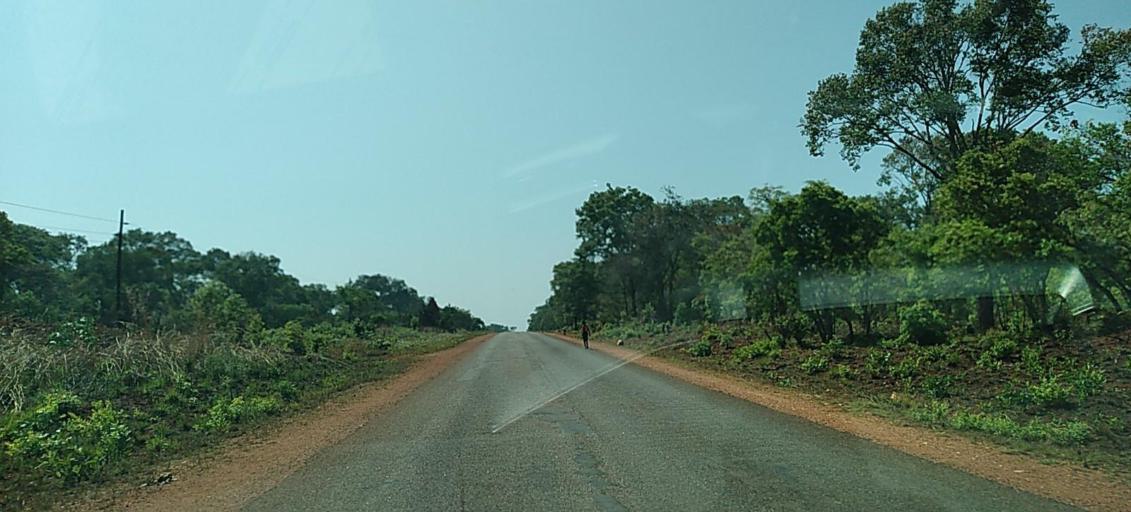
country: ZM
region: North-Western
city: Solwezi
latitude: -12.1306
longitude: 25.5283
